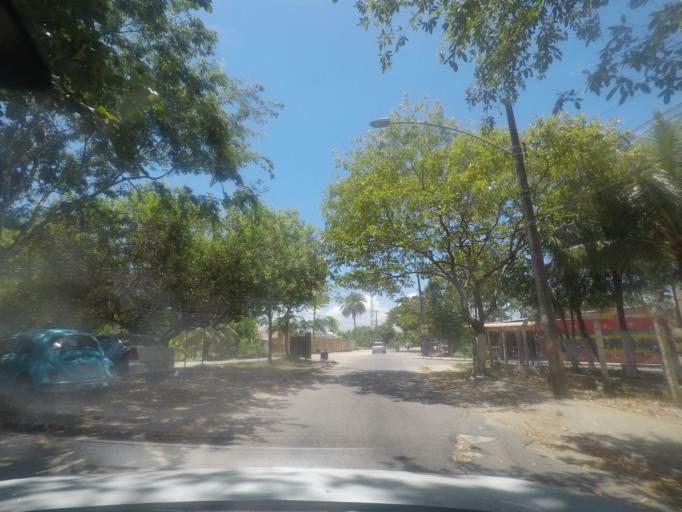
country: BR
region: Rio de Janeiro
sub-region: Itaguai
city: Itaguai
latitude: -22.9096
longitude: -43.6939
